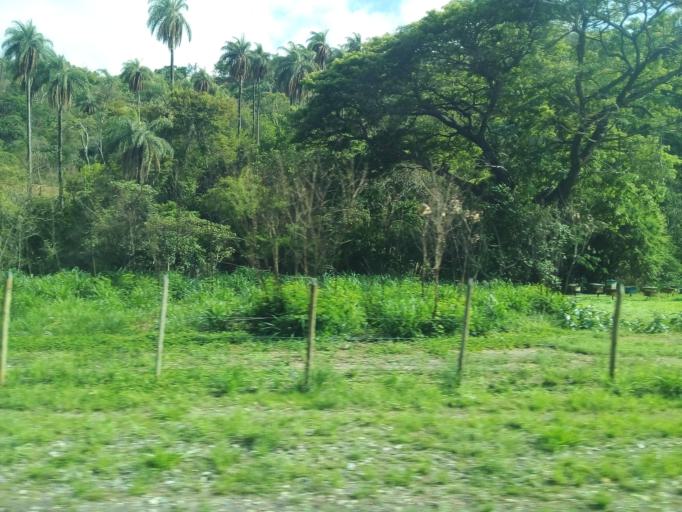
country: BR
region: Minas Gerais
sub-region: Raposos
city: Raposos
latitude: -19.8696
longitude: -43.8314
